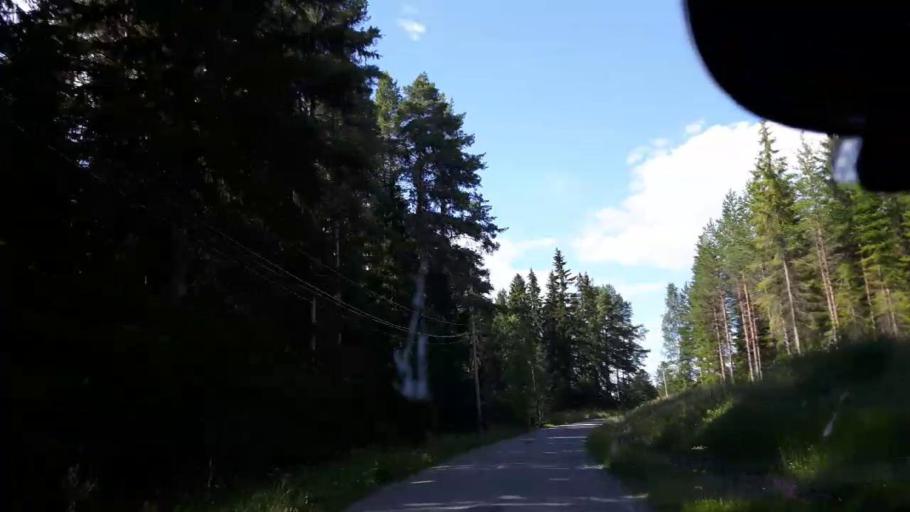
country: SE
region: Jaemtland
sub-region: Braecke Kommun
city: Braecke
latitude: 62.8657
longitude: 15.2719
